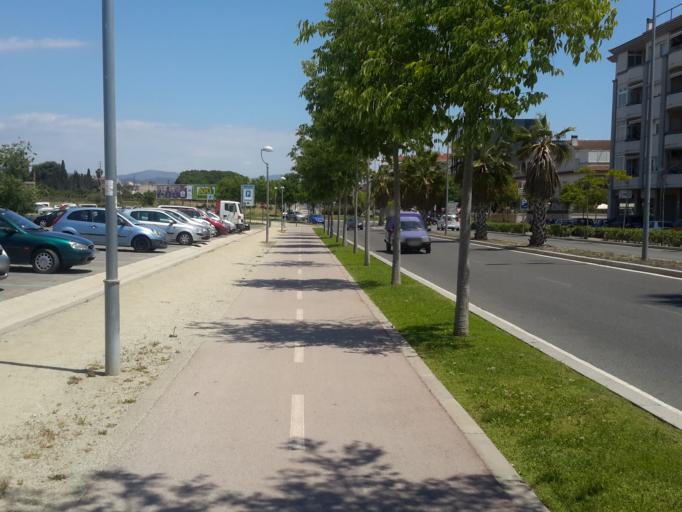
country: ES
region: Catalonia
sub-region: Provincia de Barcelona
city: Vilanova i la Geltru
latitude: 41.2261
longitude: 1.7137
